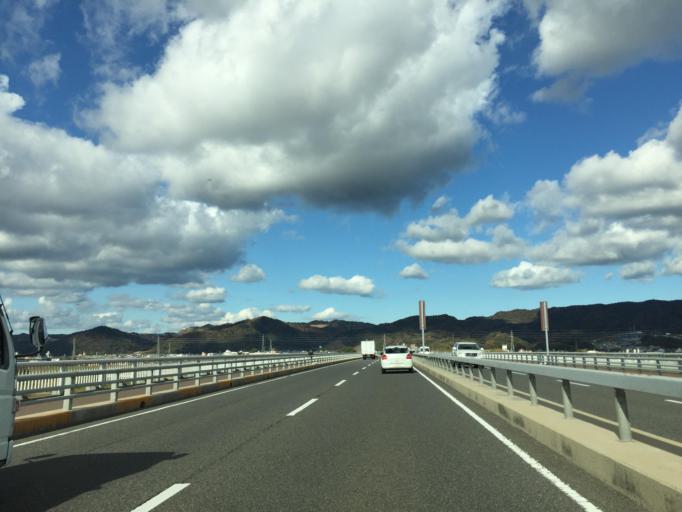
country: JP
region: Wakayama
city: Wakayama-shi
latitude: 34.2453
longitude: 135.1761
